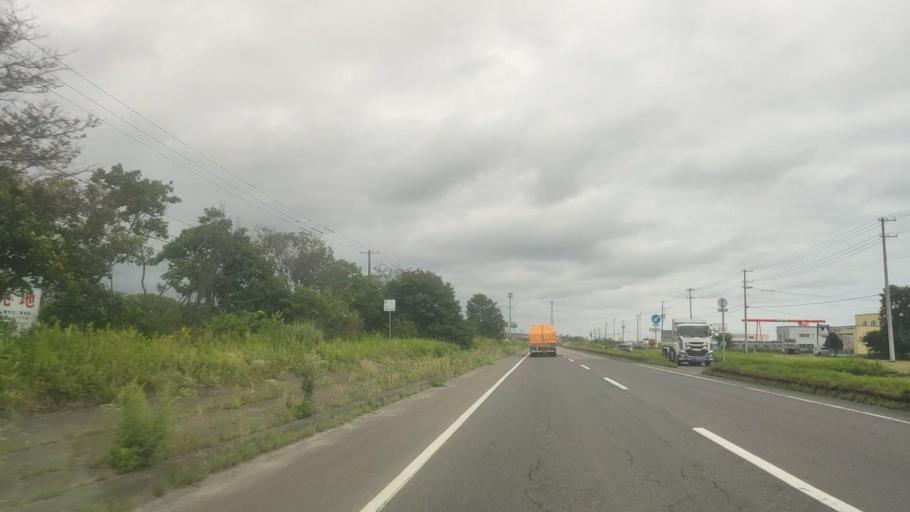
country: JP
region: Hokkaido
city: Shiraoi
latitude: 42.5342
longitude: 141.3283
